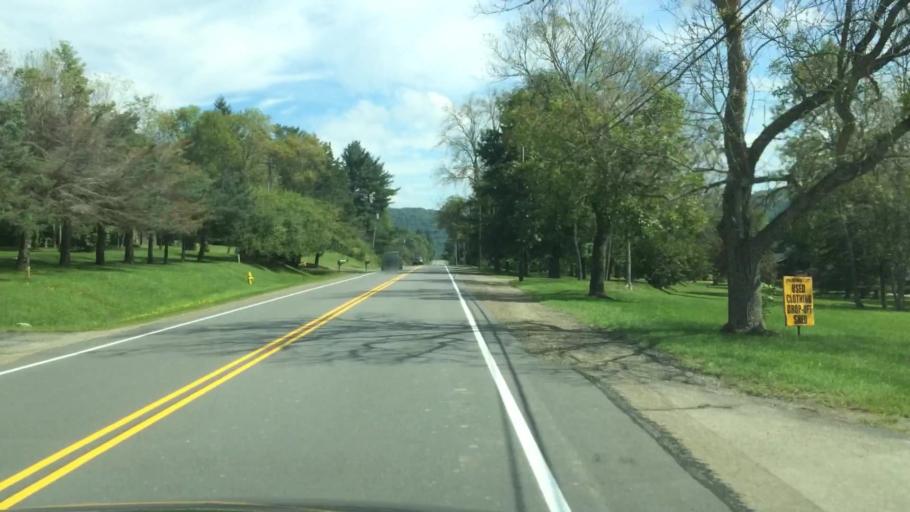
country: US
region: Pennsylvania
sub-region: McKean County
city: Bradford
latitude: 41.9107
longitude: -78.6335
